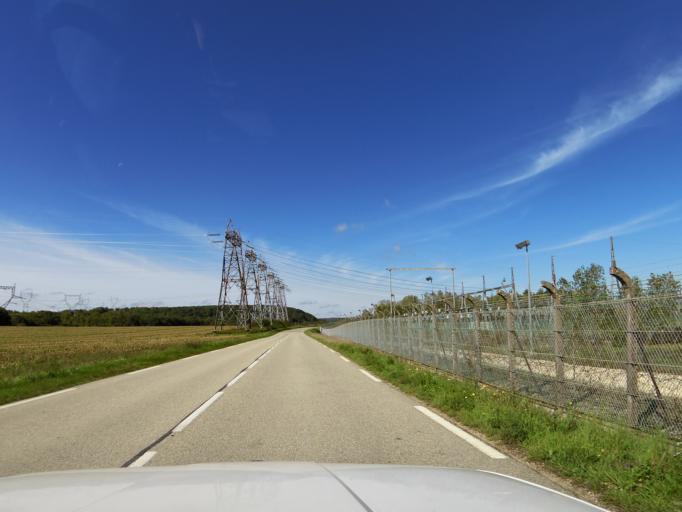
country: FR
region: Rhone-Alpes
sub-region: Departement de l'Isere
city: Creys-Mepieu
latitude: 45.7540
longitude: 5.4680
